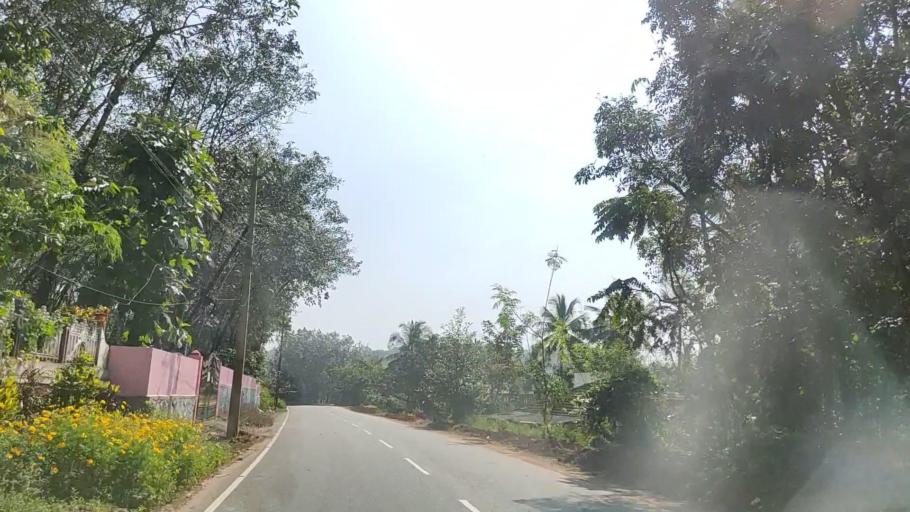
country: IN
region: Kerala
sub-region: Kollam
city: Punalur
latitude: 8.9254
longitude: 77.0638
